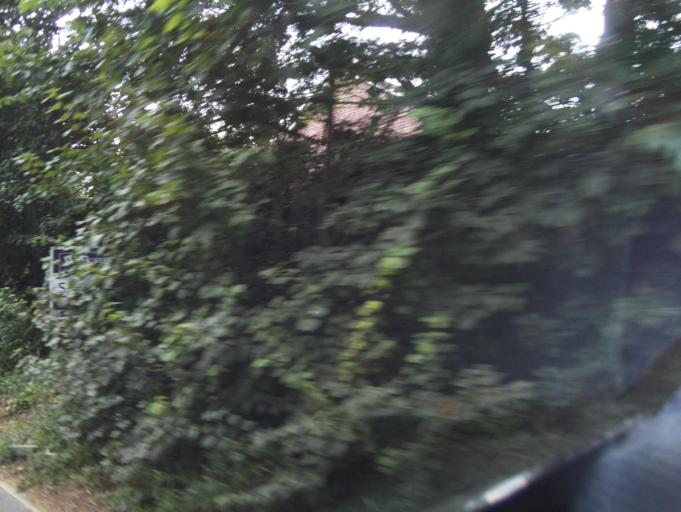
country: GB
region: England
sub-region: Hampshire
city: Milford on Sea
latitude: 50.7295
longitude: -1.5886
